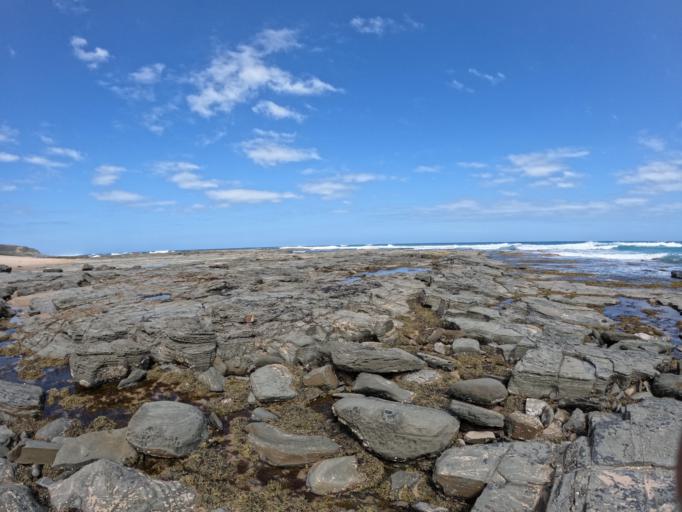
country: AU
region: Victoria
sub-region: Colac-Otway
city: Apollo Bay
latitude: -38.7927
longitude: 143.6235
